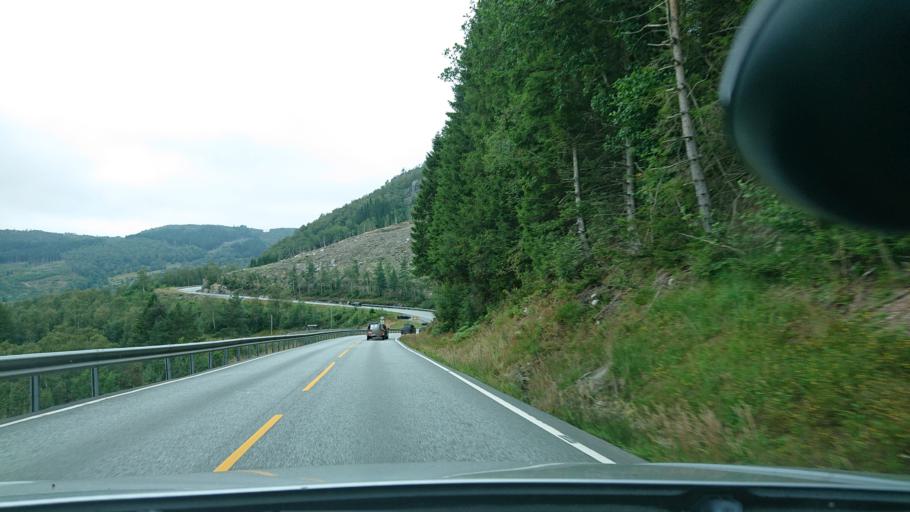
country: NO
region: Rogaland
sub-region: Hjelmeland
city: Hjelmelandsvagen
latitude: 59.1691
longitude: 6.1405
